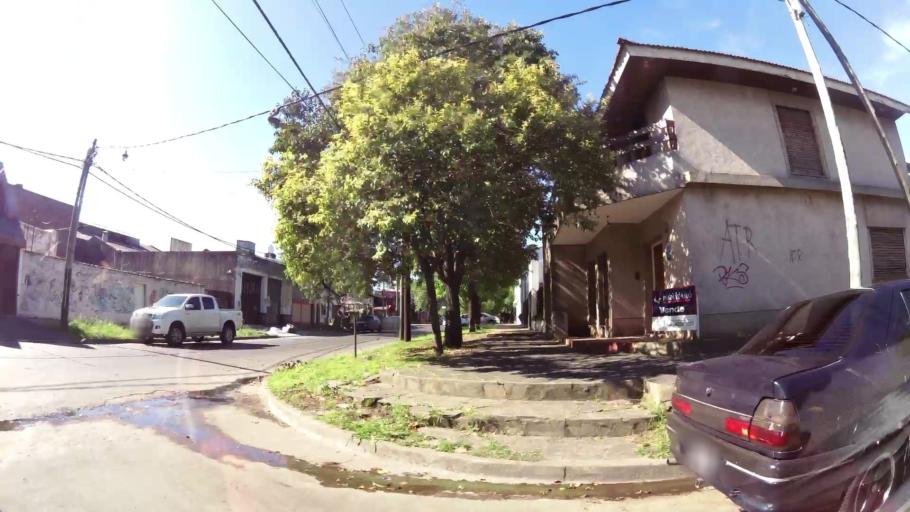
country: AR
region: Buenos Aires
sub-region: Partido de Lomas de Zamora
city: Lomas de Zamora
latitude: -34.7627
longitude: -58.4168
